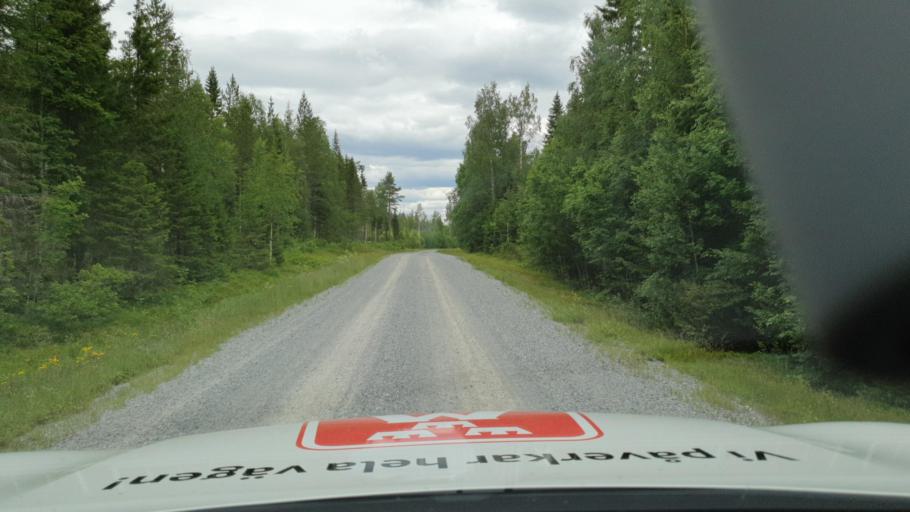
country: SE
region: Vaesterbotten
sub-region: Nordmalings Kommun
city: Nordmaling
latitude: 63.7288
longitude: 19.4264
